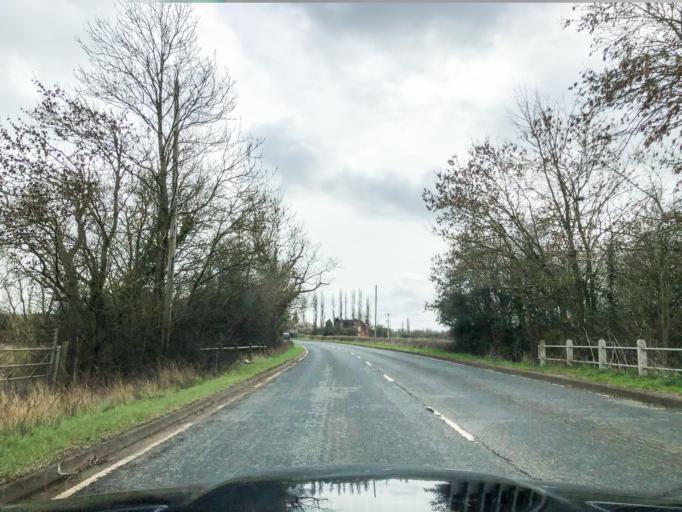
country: GB
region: England
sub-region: Warwickshire
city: Harbury
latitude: 52.1746
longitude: -1.4561
